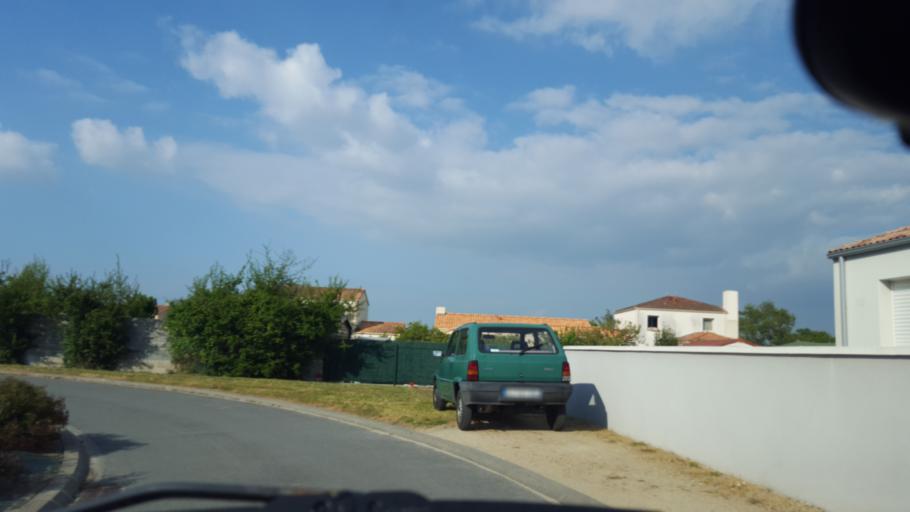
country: FR
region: Pays de la Loire
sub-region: Departement de la Loire-Atlantique
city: Saint-Philbert-de-Grand-Lieu
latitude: 47.0288
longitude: -1.6316
